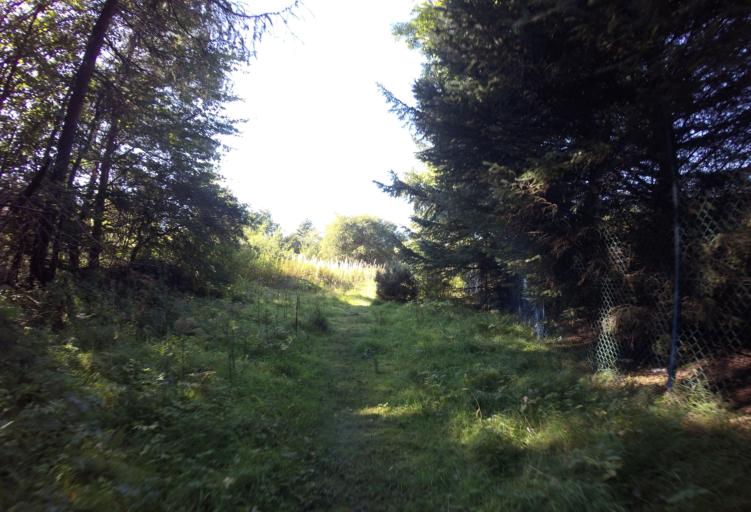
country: GB
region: Scotland
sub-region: West Lothian
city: West Calder
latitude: 55.8935
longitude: -3.5706
